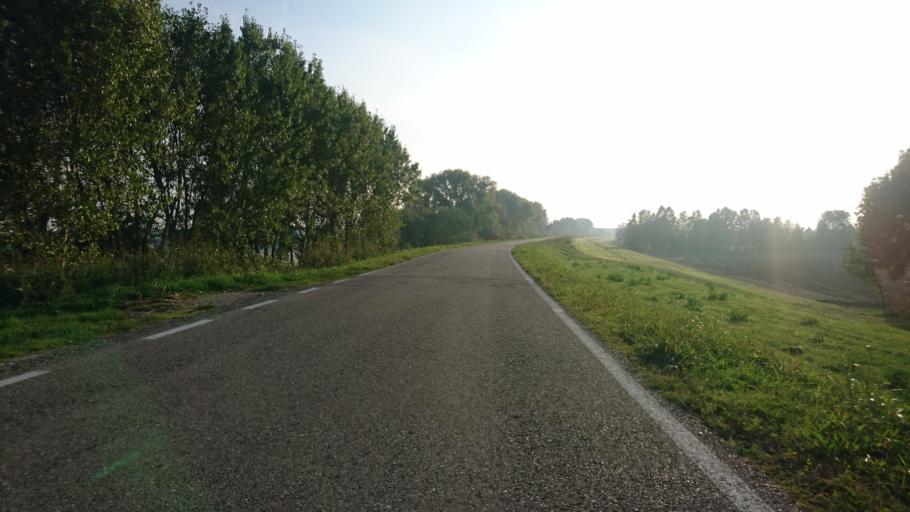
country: IT
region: Emilia-Romagna
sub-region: Provincia di Ferrara
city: Francolino
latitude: 44.9047
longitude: 11.6482
